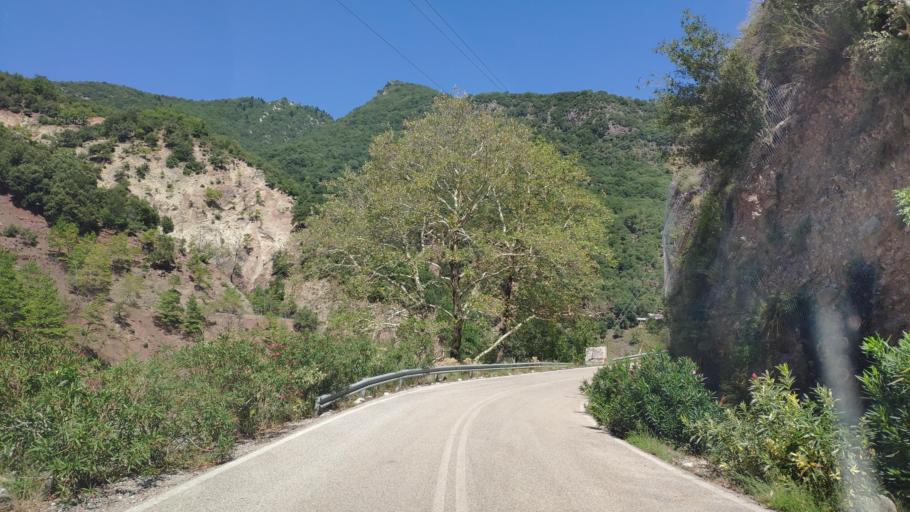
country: GR
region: Central Greece
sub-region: Nomos Evrytanias
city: Kerasochori
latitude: 39.0525
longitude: 21.6027
